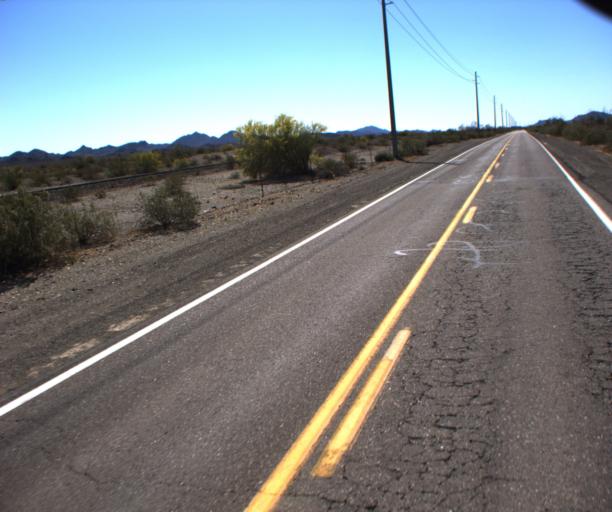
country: US
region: Arizona
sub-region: La Paz County
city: Salome
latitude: 33.7813
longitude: -113.8077
